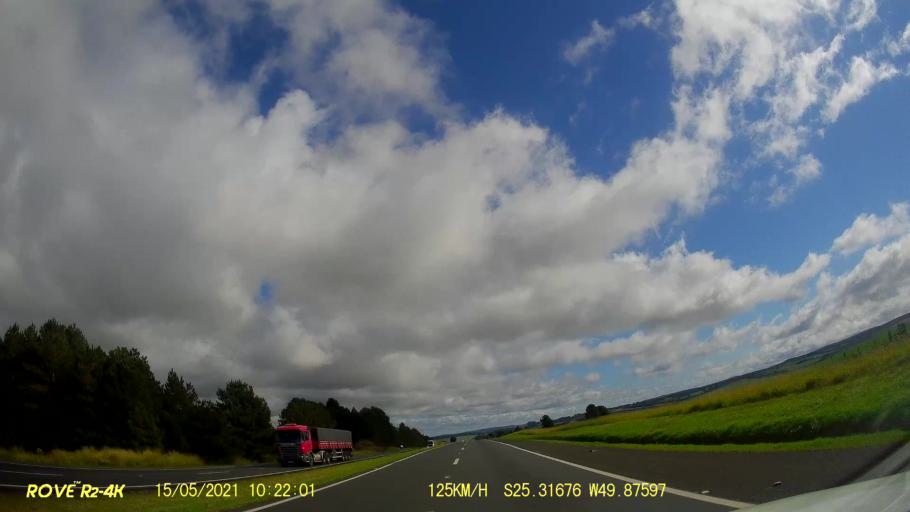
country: BR
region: Parana
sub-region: Palmeira
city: Palmeira
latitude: -25.3170
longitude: -49.8759
